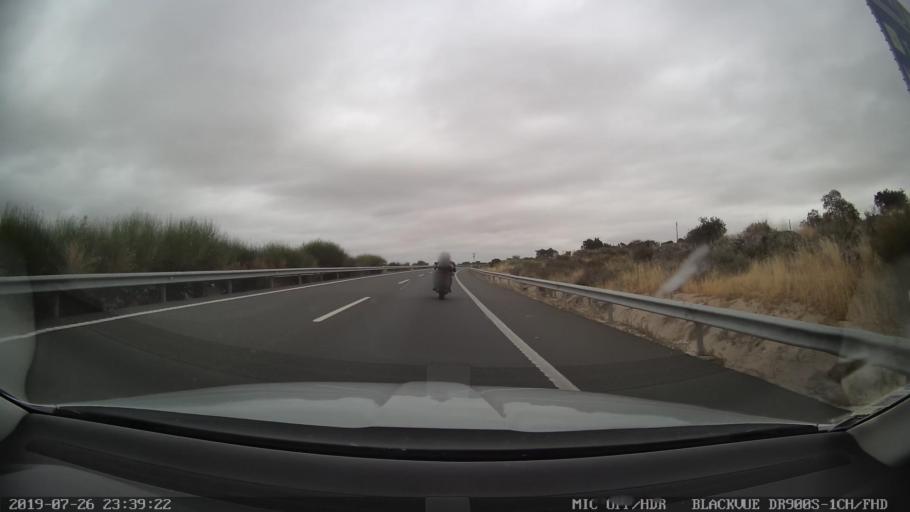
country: ES
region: Extremadura
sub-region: Provincia de Caceres
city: Trujillo
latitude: 39.4479
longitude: -5.8735
